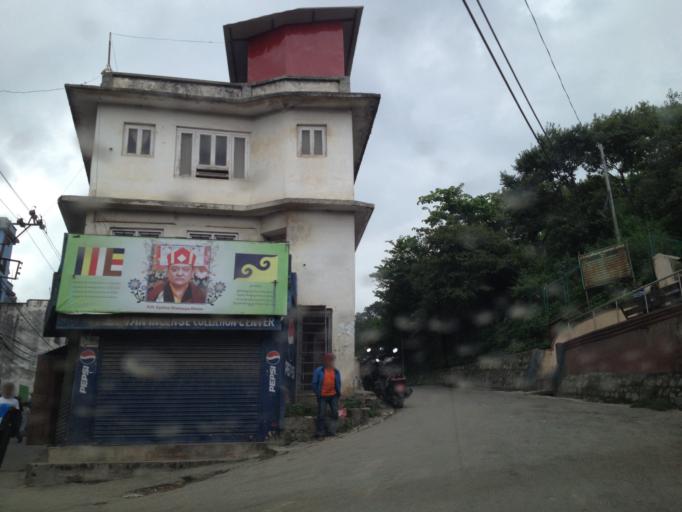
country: NP
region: Central Region
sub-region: Bagmati Zone
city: Kathmandu
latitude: 27.7131
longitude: 85.2897
